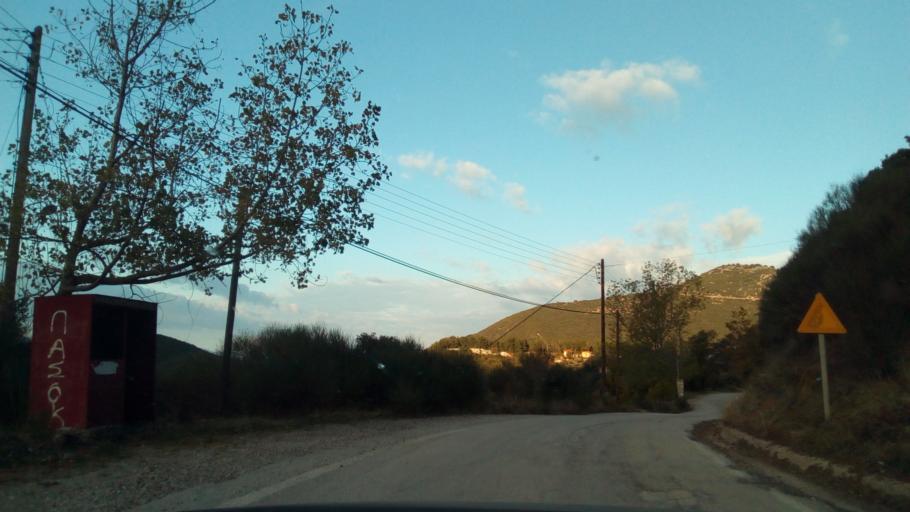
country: GR
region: West Greece
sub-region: Nomos Aitolias kai Akarnanias
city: Nafpaktos
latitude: 38.5296
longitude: 21.8295
